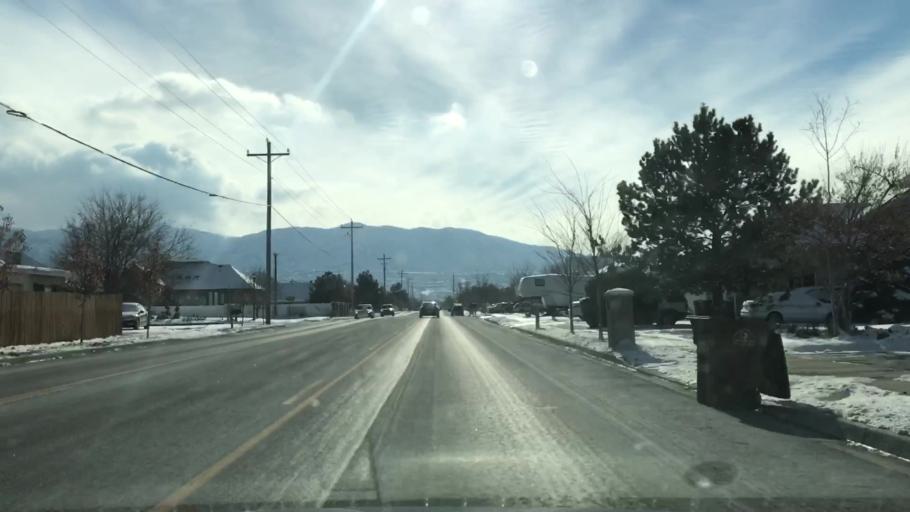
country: US
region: Utah
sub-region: Salt Lake County
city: Draper
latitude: 40.5221
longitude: -111.8818
